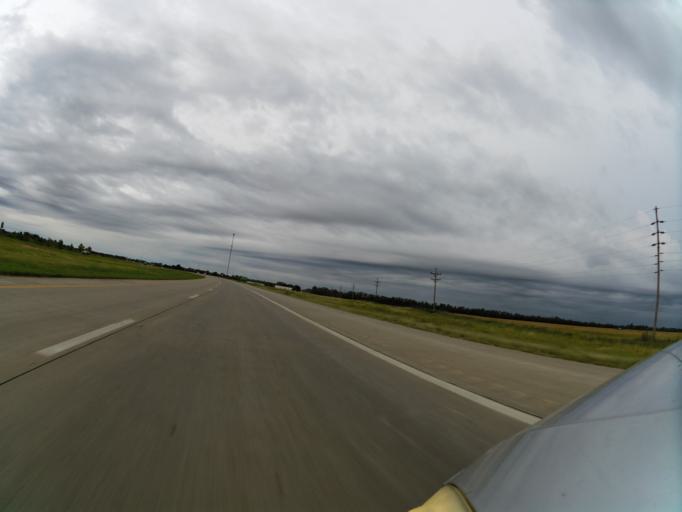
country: US
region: Kansas
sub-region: Reno County
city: South Hutchinson
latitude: 37.9774
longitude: -97.9403
